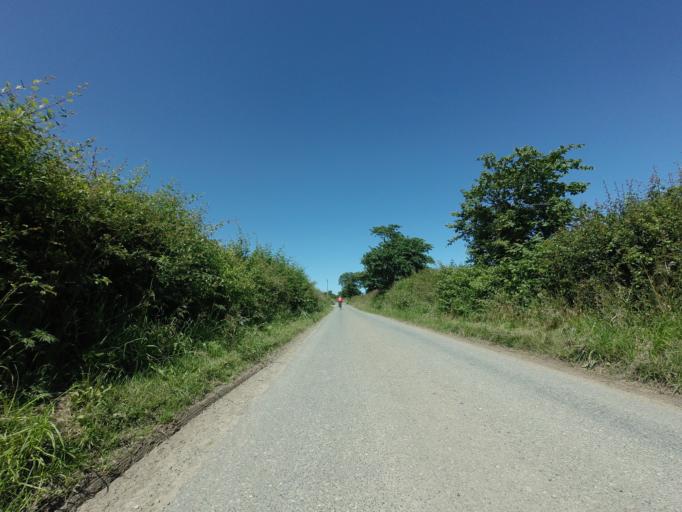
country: GB
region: Scotland
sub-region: Aberdeenshire
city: Macduff
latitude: 57.6351
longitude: -2.4909
